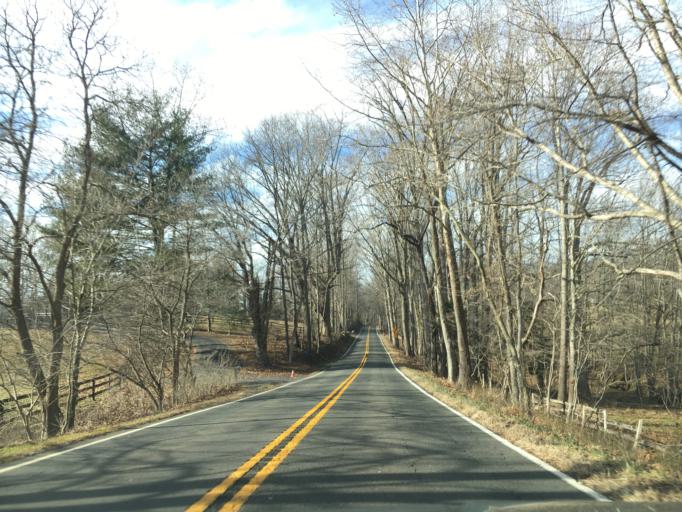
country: US
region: Virginia
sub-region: Fauquier County
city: Warrenton
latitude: 38.7100
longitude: -77.9216
